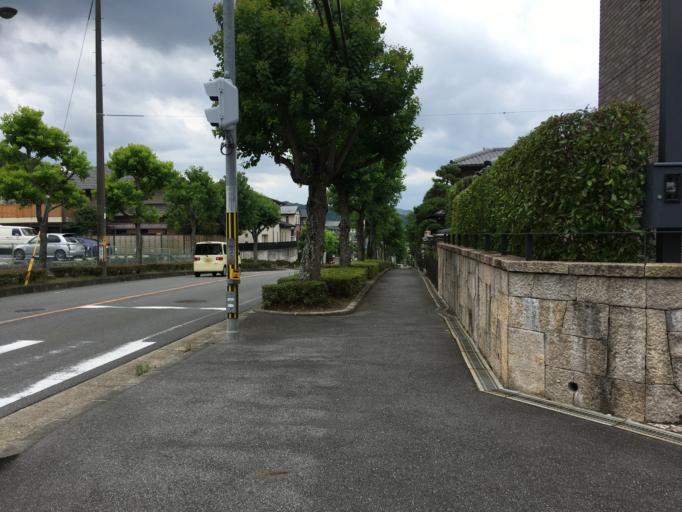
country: JP
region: Nara
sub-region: Ikoma-shi
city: Ikoma
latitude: 34.6777
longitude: 135.7188
